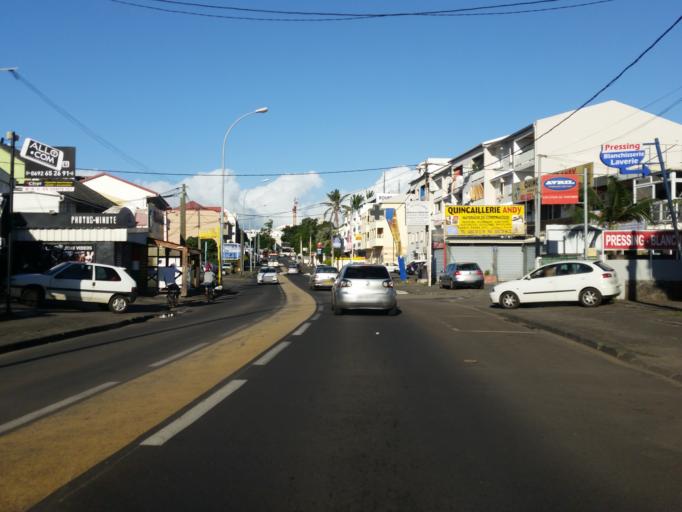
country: RE
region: Reunion
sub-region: Reunion
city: Saint-Denis
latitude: -20.8953
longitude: 55.4890
